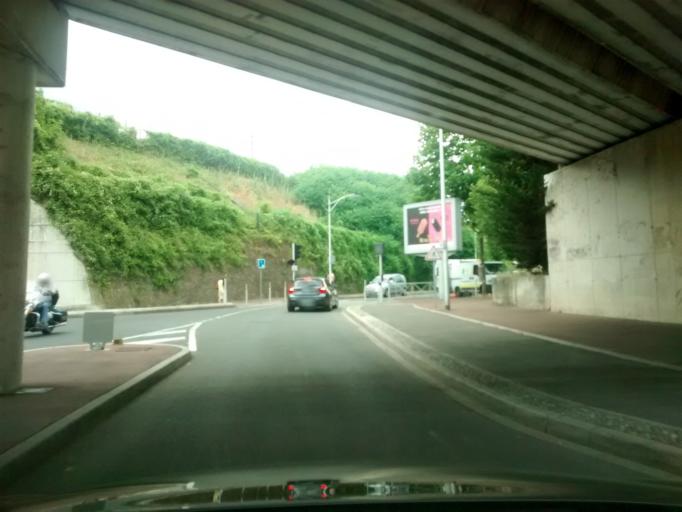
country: FR
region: Ile-de-France
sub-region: Departement des Hauts-de-Seine
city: Boulogne-Billancourt
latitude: 48.8266
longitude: 2.2616
